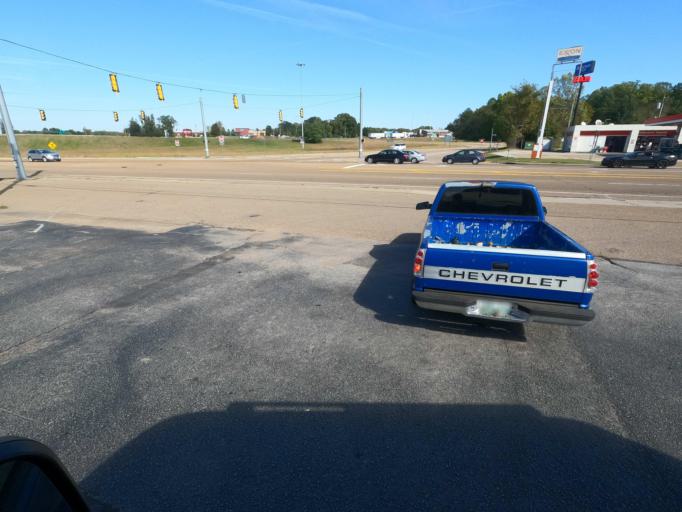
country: US
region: Tennessee
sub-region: Madison County
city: Jackson
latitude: 35.6553
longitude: -88.8734
